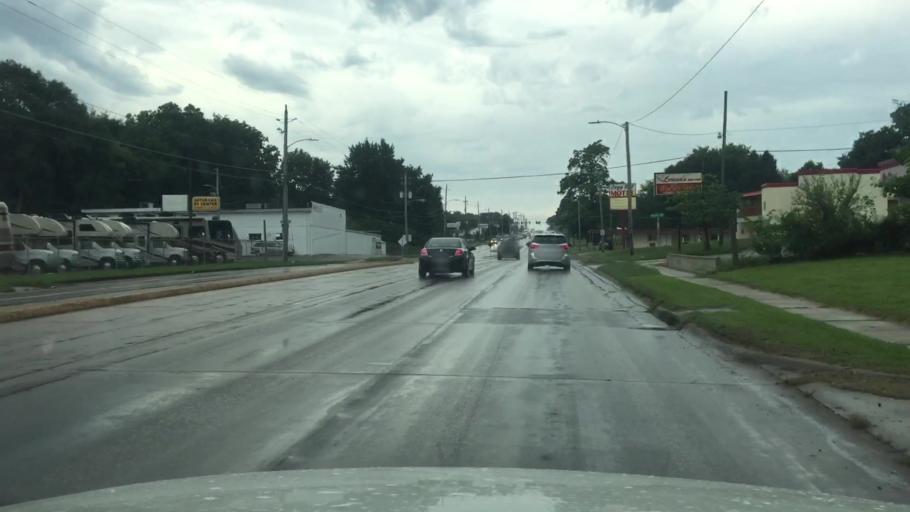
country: US
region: Iowa
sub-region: Polk County
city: Des Moines
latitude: 41.5667
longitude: -93.5970
